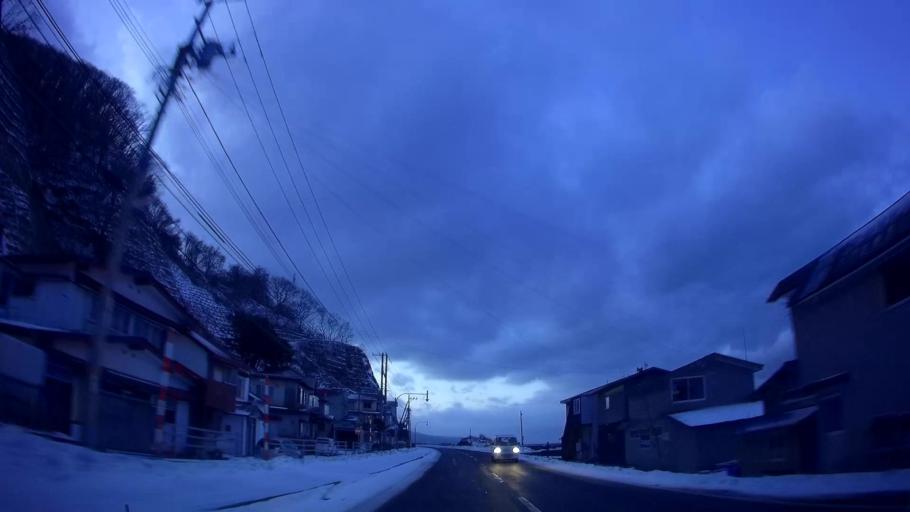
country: JP
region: Hokkaido
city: Hakodate
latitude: 41.8886
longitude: 141.0618
